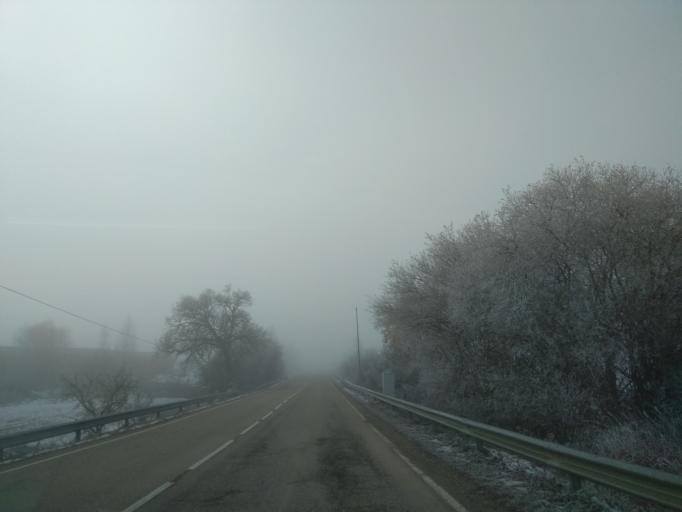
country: ES
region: Castille and Leon
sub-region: Provincia de Burgos
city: Espinosa de los Monteros
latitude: 43.0269
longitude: -3.5041
